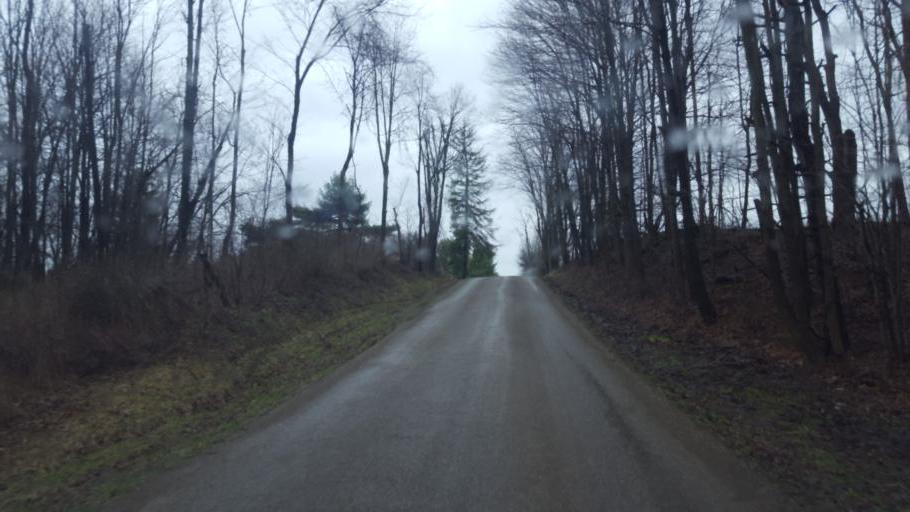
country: US
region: Ohio
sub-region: Sandusky County
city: Bellville
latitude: 40.5771
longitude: -82.5803
